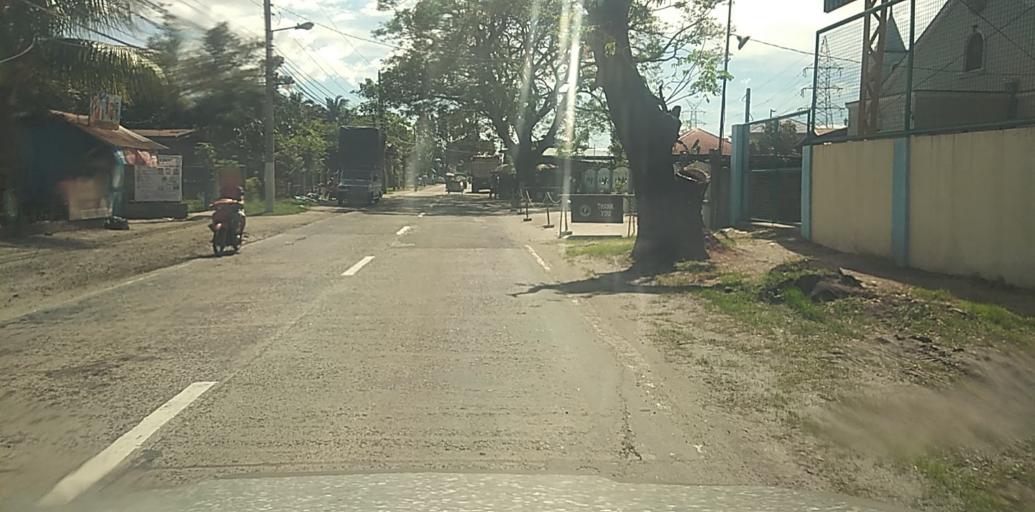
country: PH
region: Central Luzon
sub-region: Province of Pampanga
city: Buensuseso
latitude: 15.1955
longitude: 120.6723
